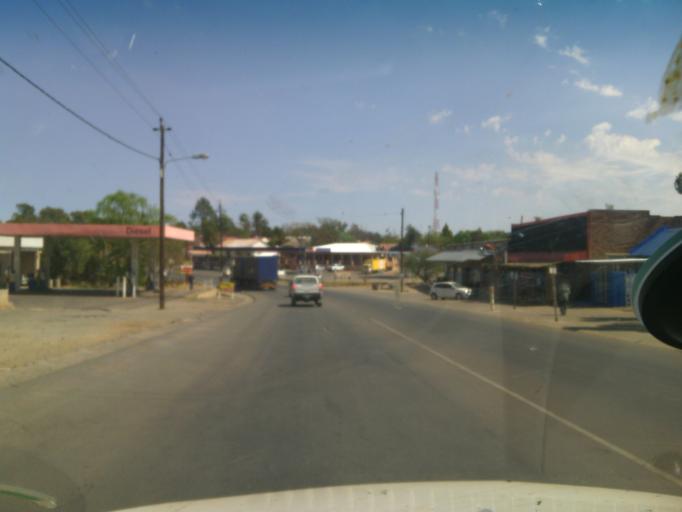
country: ZA
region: Northern Cape
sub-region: Frances Baard District Municipality
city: Barkly West
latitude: -28.5367
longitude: 24.5247
